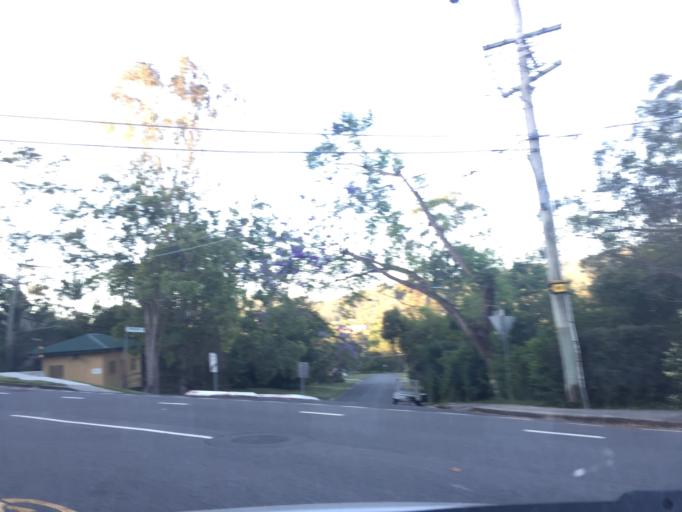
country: AU
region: Queensland
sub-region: Brisbane
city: Taringa
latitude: -27.4495
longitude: 152.9467
